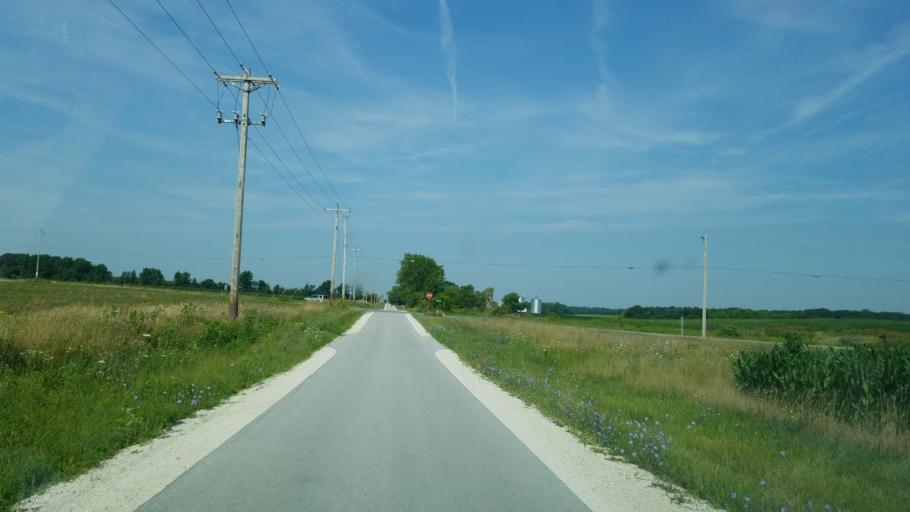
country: US
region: Ohio
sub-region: Sandusky County
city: Green Springs
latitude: 41.1393
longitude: -83.0028
